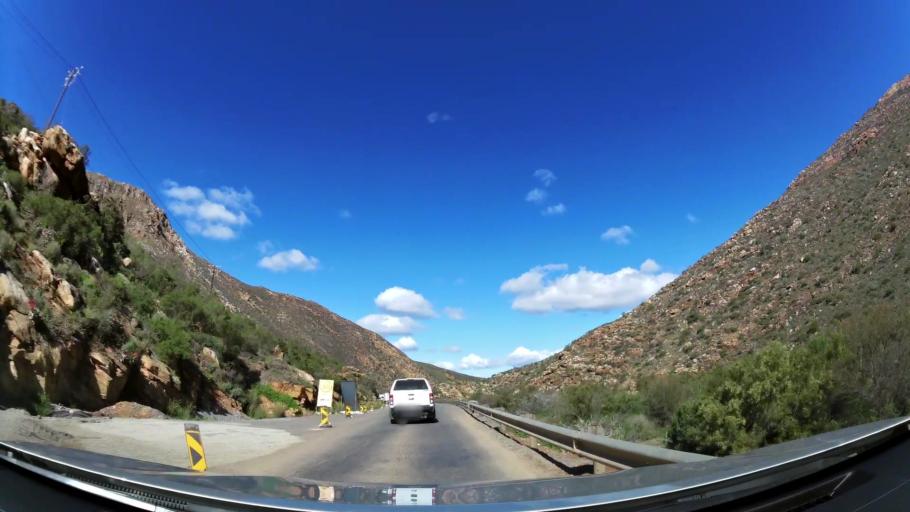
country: ZA
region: Western Cape
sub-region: Cape Winelands District Municipality
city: Ashton
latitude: -33.8166
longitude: 20.0899
